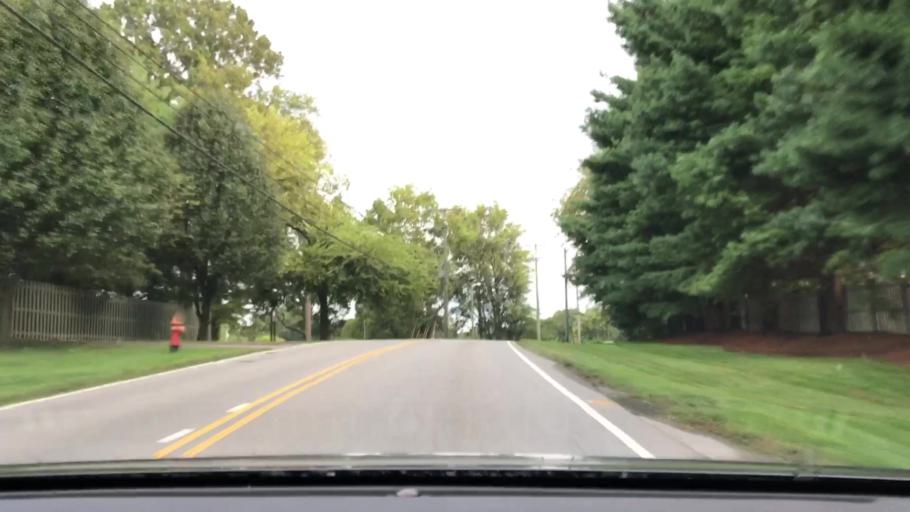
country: US
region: Tennessee
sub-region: Williamson County
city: Brentwood Estates
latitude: 36.0206
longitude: -86.7425
